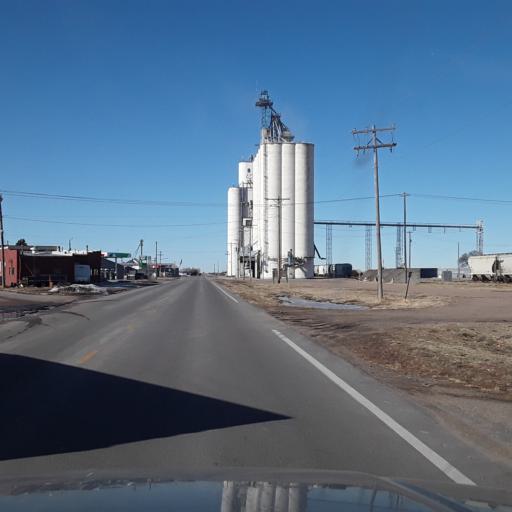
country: US
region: Nebraska
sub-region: Gosper County
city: Elwood
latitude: 40.5275
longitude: -99.6320
